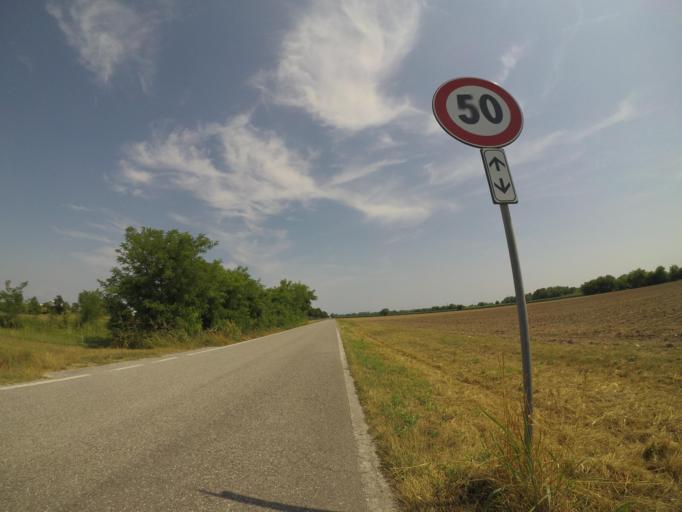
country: IT
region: Friuli Venezia Giulia
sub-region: Provincia di Pordenone
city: Rosa
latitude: 45.9327
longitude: 12.8879
